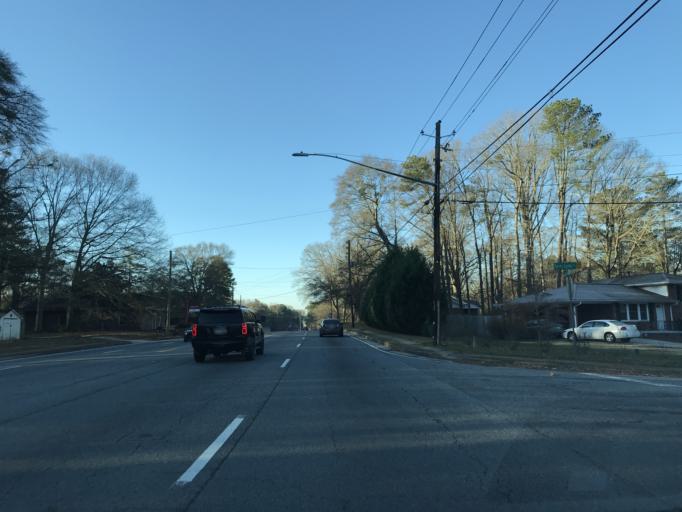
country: US
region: Georgia
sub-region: DeKalb County
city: Clarkston
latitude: 33.8352
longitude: -84.2418
